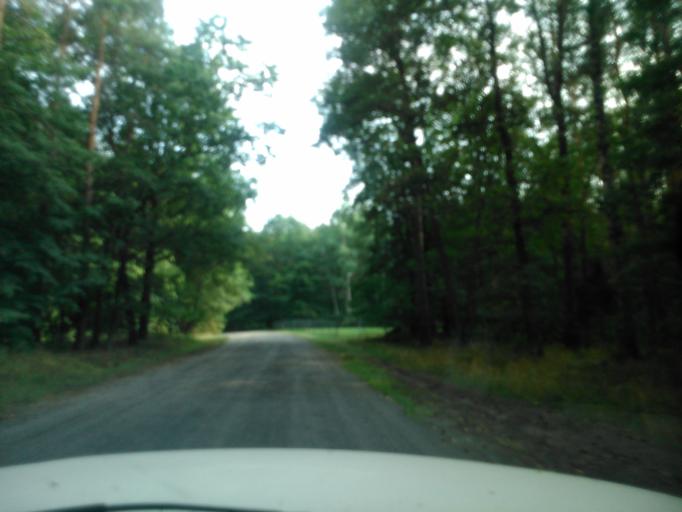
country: PL
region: Kujawsko-Pomorskie
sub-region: Powiat golubsko-dobrzynski
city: Golub-Dobrzyn
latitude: 53.1515
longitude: 19.1291
